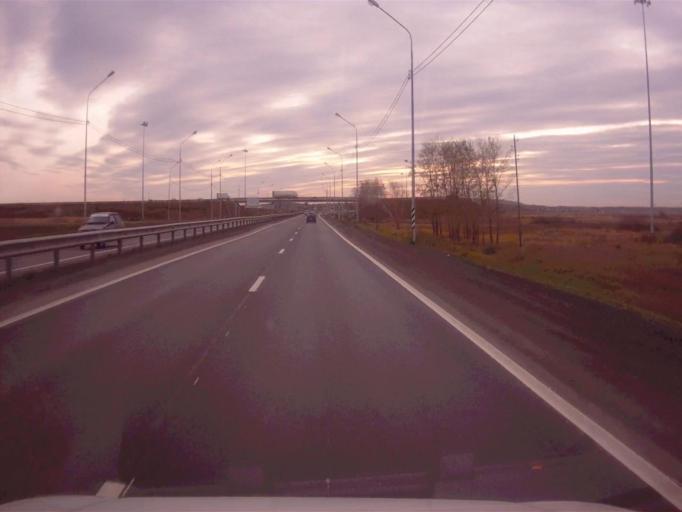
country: RU
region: Chelyabinsk
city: Roza
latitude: 54.9989
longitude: 61.4518
